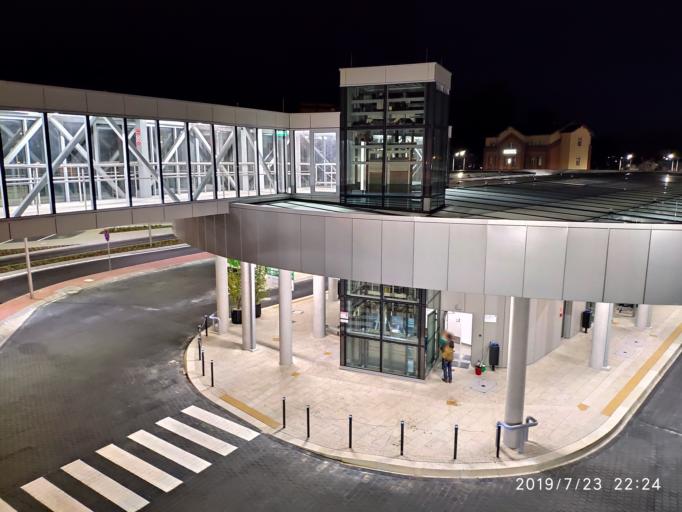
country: PL
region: Lubusz
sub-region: Zielona Gora
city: Zielona Gora
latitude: 51.9471
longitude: 15.5172
